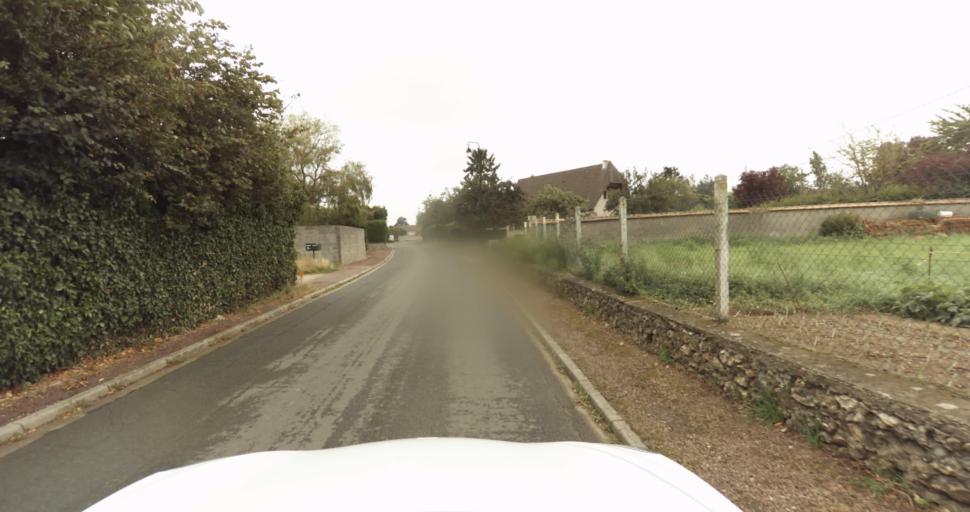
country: FR
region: Haute-Normandie
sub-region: Departement de l'Eure
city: Aviron
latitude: 49.0774
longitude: 1.0864
